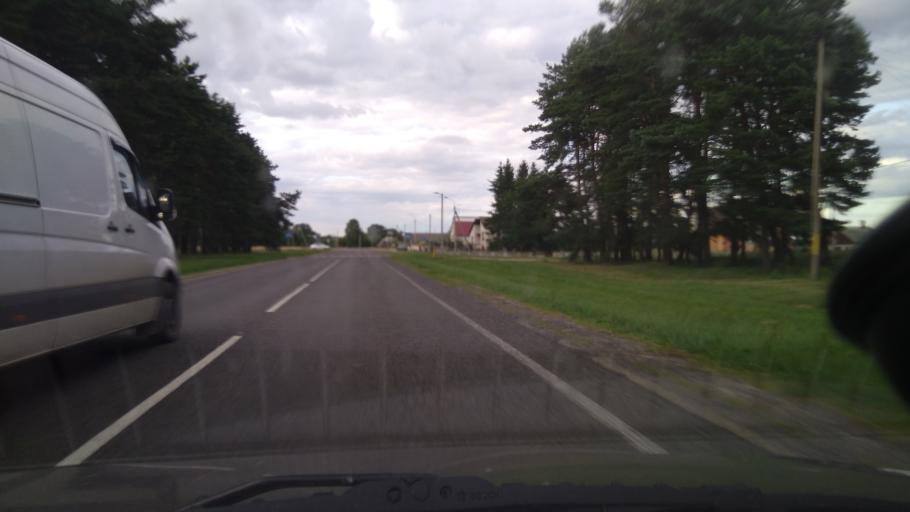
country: BY
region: Grodnenskaya
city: Shchuchin
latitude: 53.4857
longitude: 24.6648
